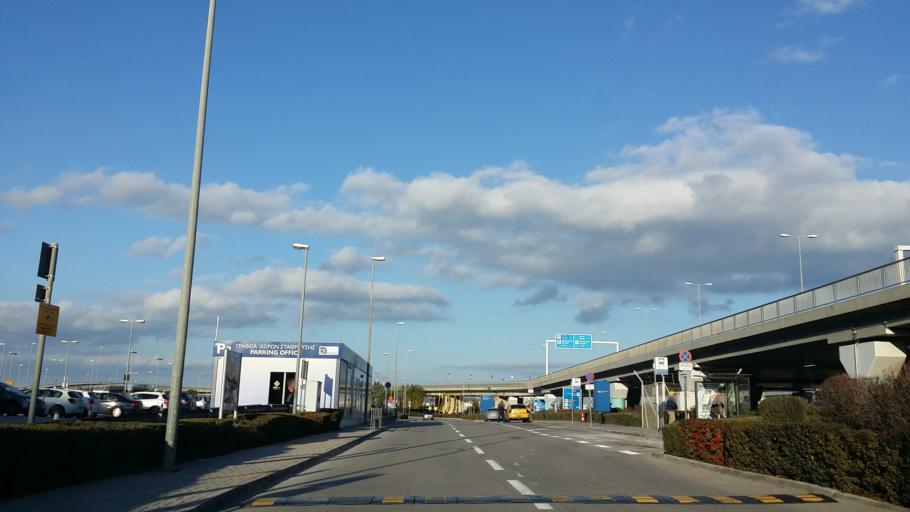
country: GR
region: Attica
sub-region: Nomarchia Anatolikis Attikis
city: Spata
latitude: 37.9376
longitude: 23.9471
